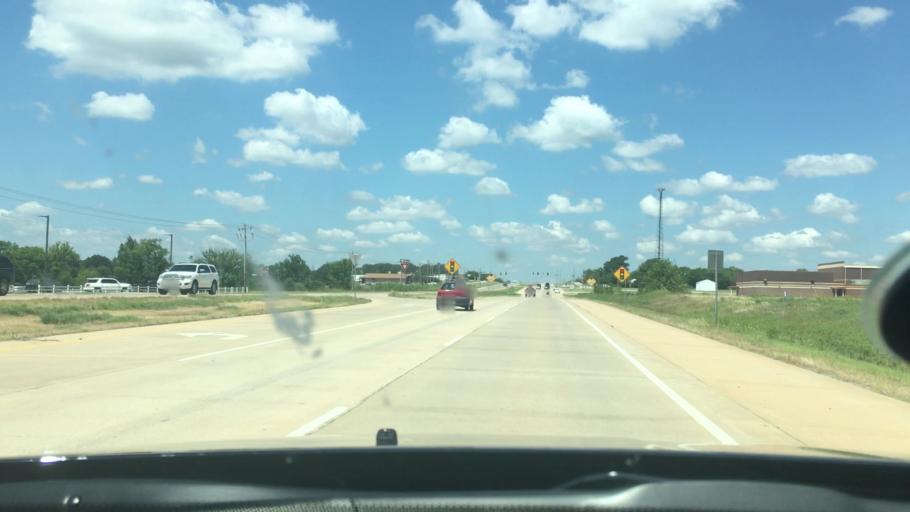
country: US
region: Oklahoma
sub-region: Carter County
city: Lone Grove
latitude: 34.1730
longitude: -97.2426
